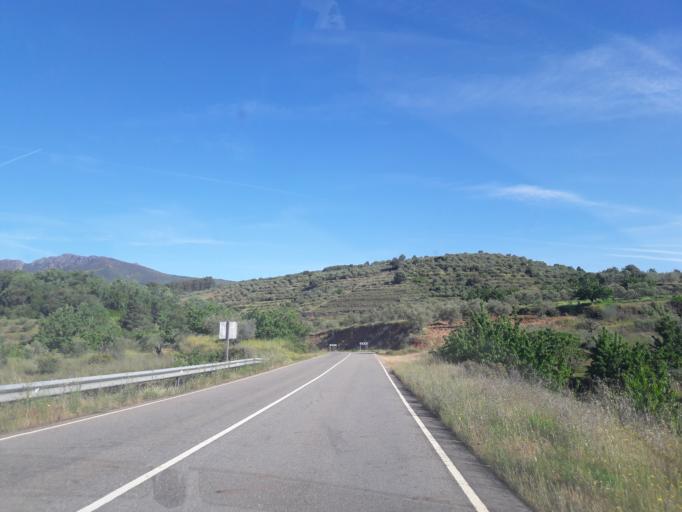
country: ES
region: Castille and Leon
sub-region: Provincia de Salamanca
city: Sotoserrano
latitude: 40.4246
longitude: -6.0359
